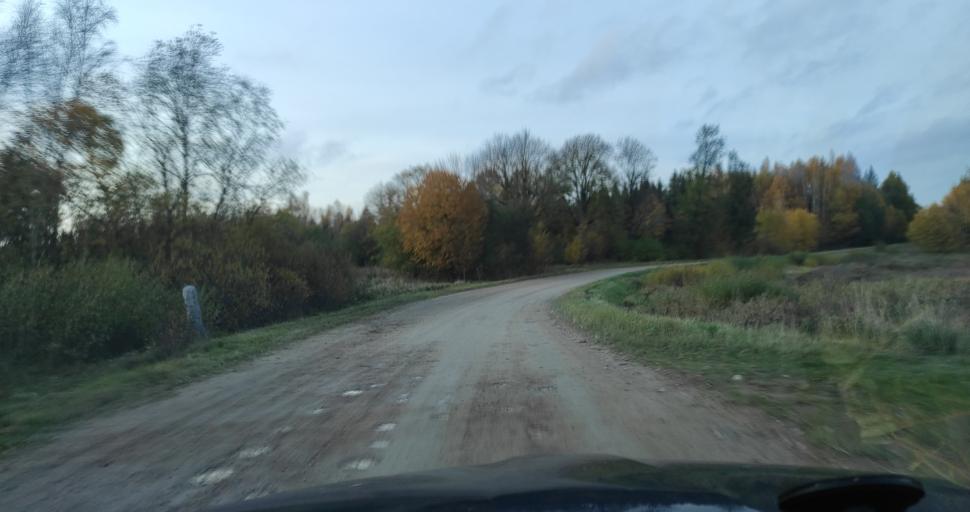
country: LV
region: Aizpute
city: Aizpute
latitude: 56.6690
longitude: 21.7923
